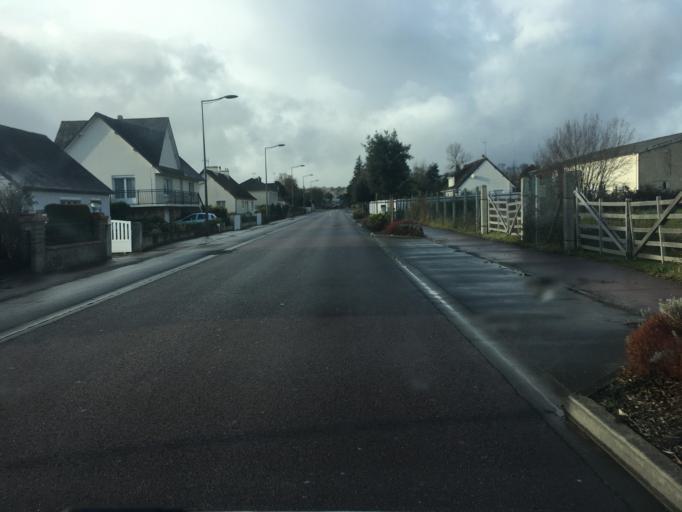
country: FR
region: Lower Normandy
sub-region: Departement de la Manche
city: Quettehou
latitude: 49.5910
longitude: -1.2927
